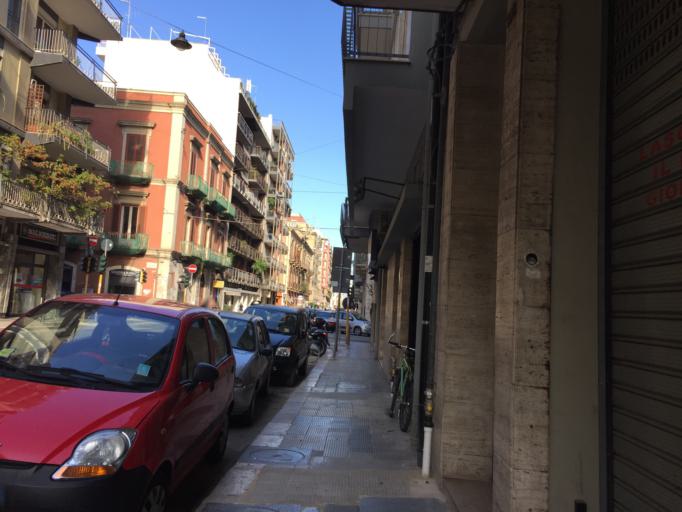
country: IT
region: Apulia
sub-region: Provincia di Bari
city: Bari
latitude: 41.1226
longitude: 16.8643
